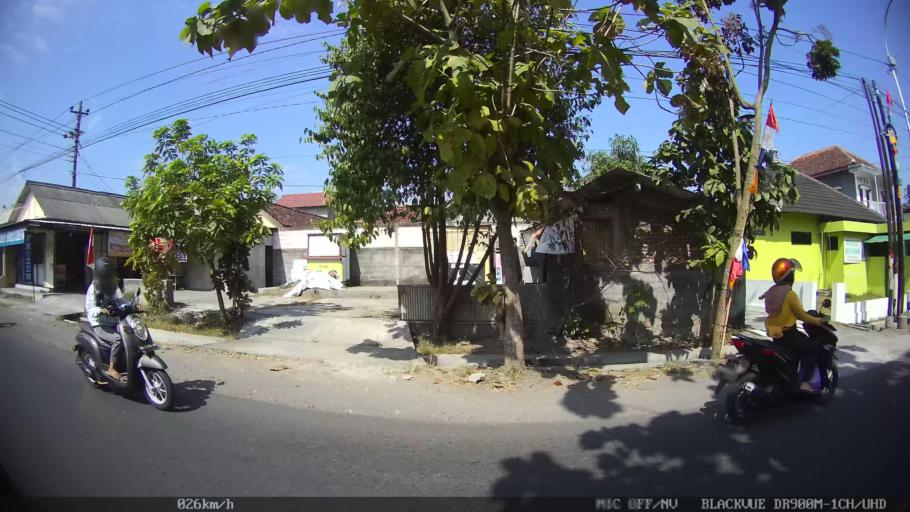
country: ID
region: Daerah Istimewa Yogyakarta
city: Sewon
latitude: -7.8991
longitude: 110.3843
